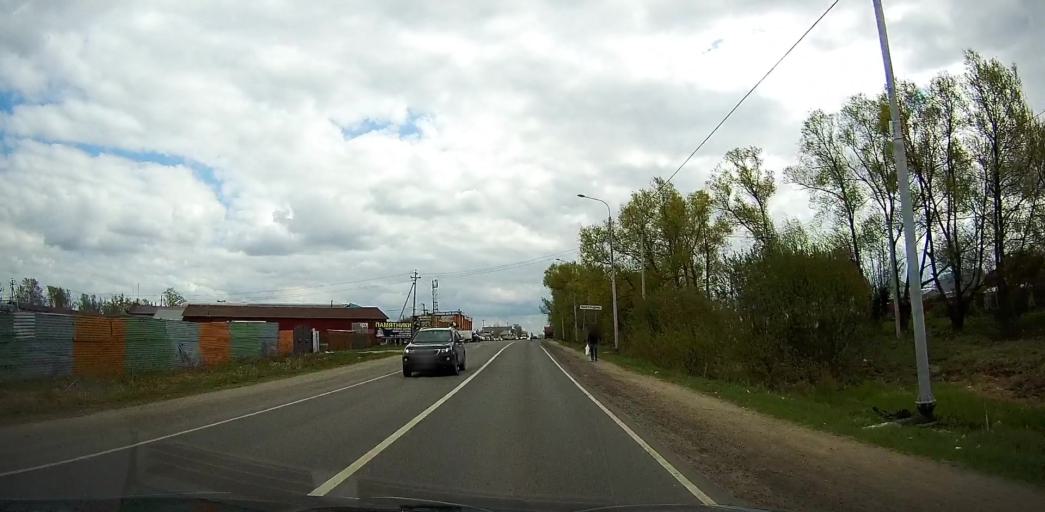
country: RU
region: Moskovskaya
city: Ashitkovo
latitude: 55.4286
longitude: 38.5471
